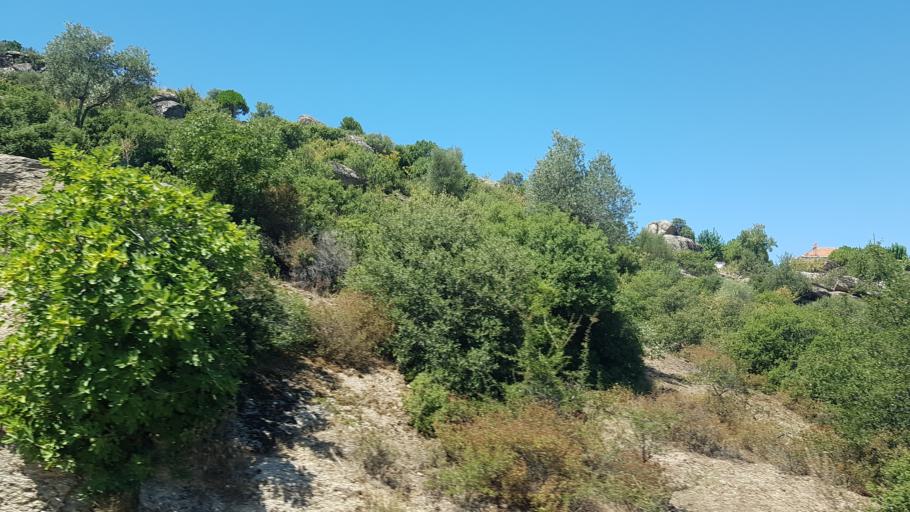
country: TR
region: Aydin
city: Akcaova
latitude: 37.4770
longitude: 28.1314
